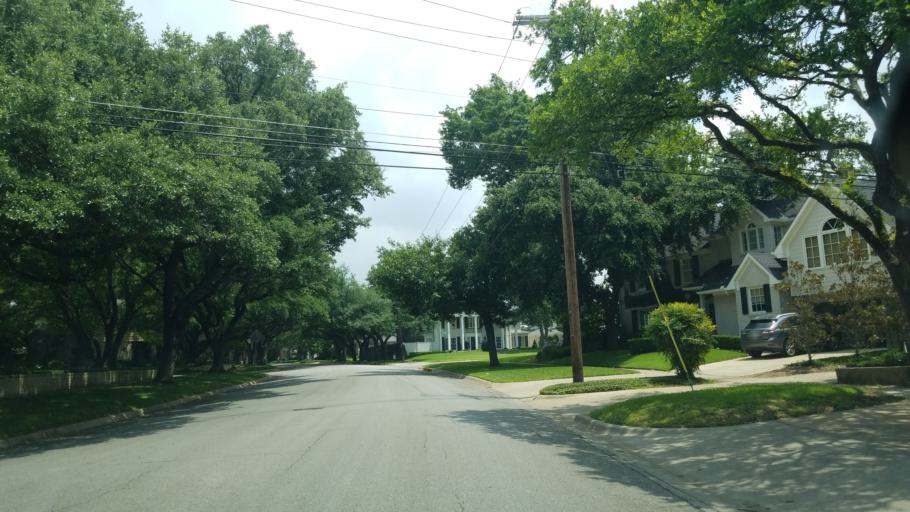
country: US
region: Texas
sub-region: Dallas County
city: University Park
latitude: 32.8419
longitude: -96.8107
